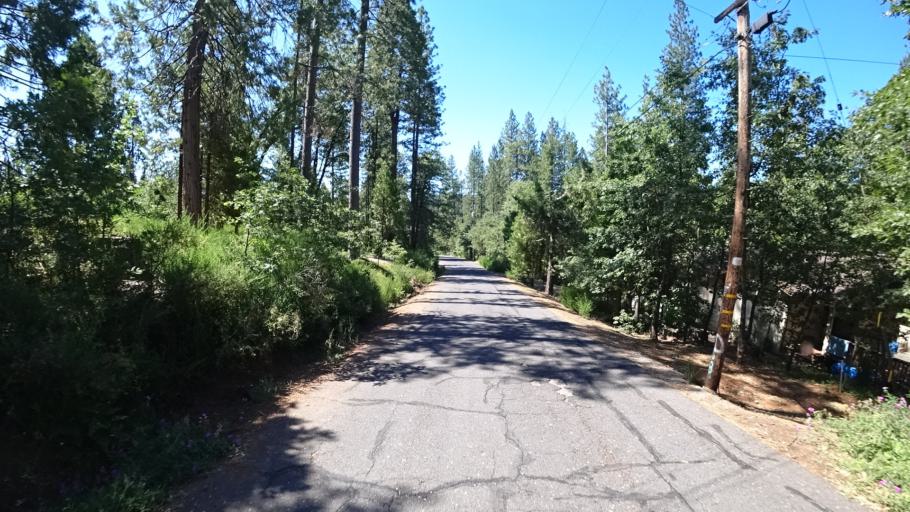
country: US
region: California
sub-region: Calaveras County
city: Arnold
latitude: 38.2384
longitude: -120.3751
